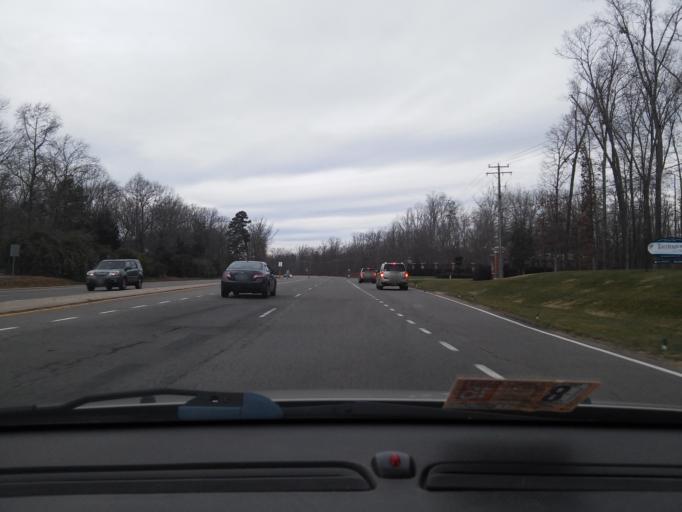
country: US
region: Virginia
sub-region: Chesterfield County
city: Bon Air
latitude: 37.5399
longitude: -77.6421
